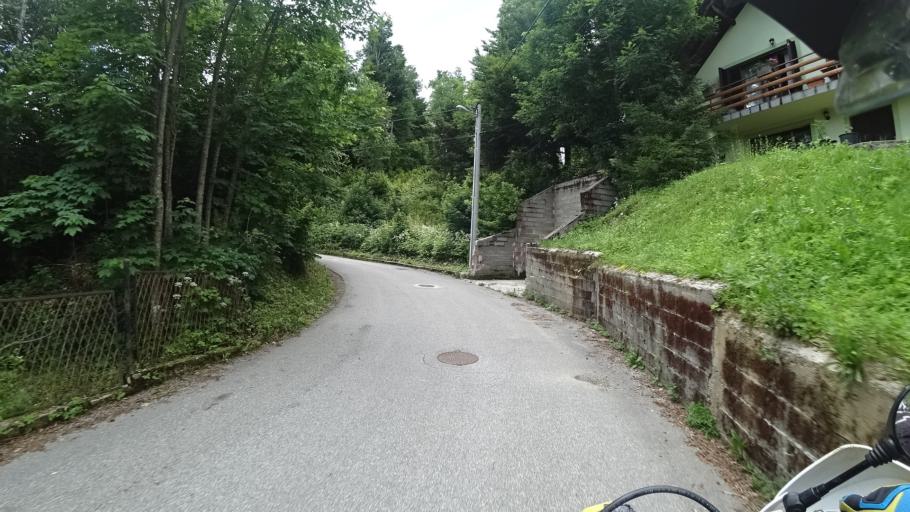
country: HR
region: Primorsko-Goranska
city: Hreljin
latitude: 45.3023
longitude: 14.7111
